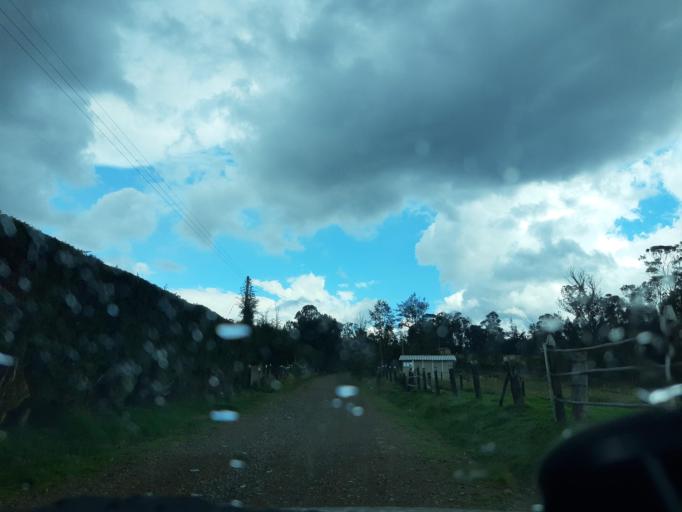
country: CO
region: Boyaca
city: Raquira
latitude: 5.4935
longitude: -73.6967
